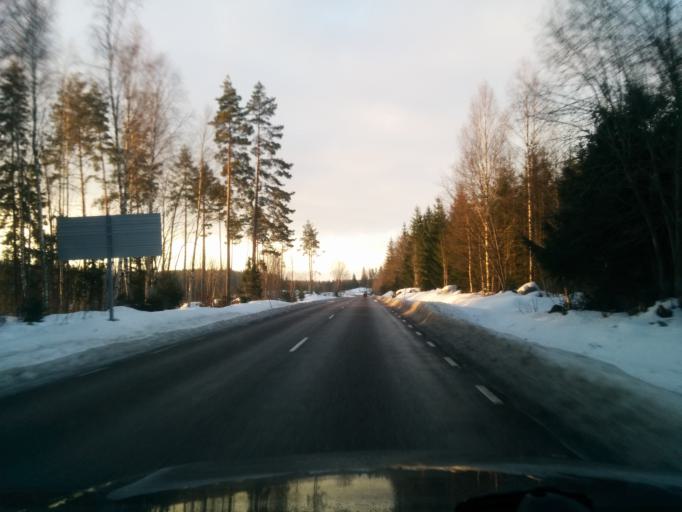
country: SE
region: Uppsala
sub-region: Tierps Kommun
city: Orbyhus
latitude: 60.2144
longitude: 17.7012
